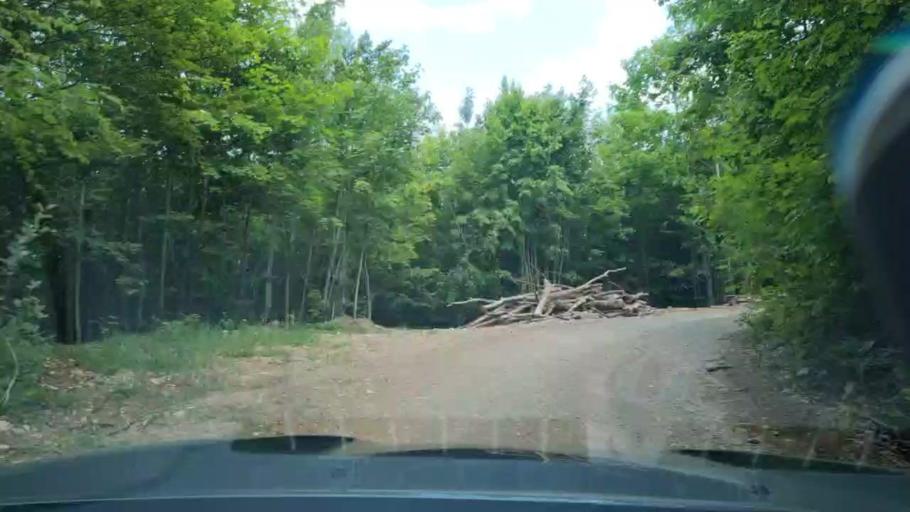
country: BA
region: Federation of Bosnia and Herzegovina
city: Bosansko Grahovo
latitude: 44.3217
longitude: 16.2446
